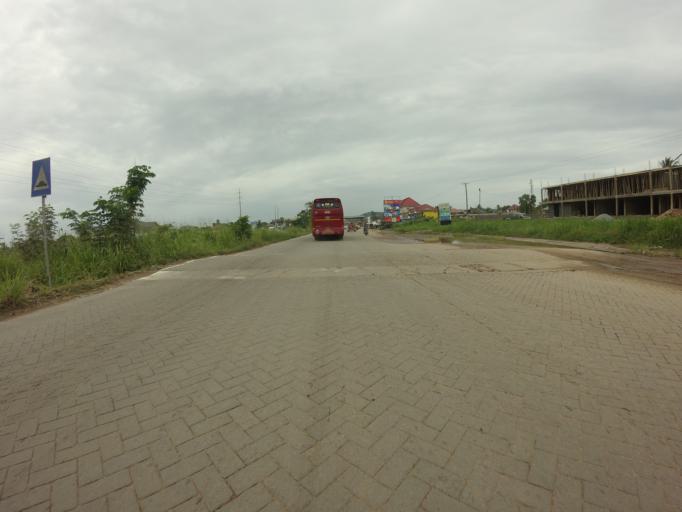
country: GH
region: Greater Accra
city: Achiaman
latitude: 5.7326
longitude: -0.3132
